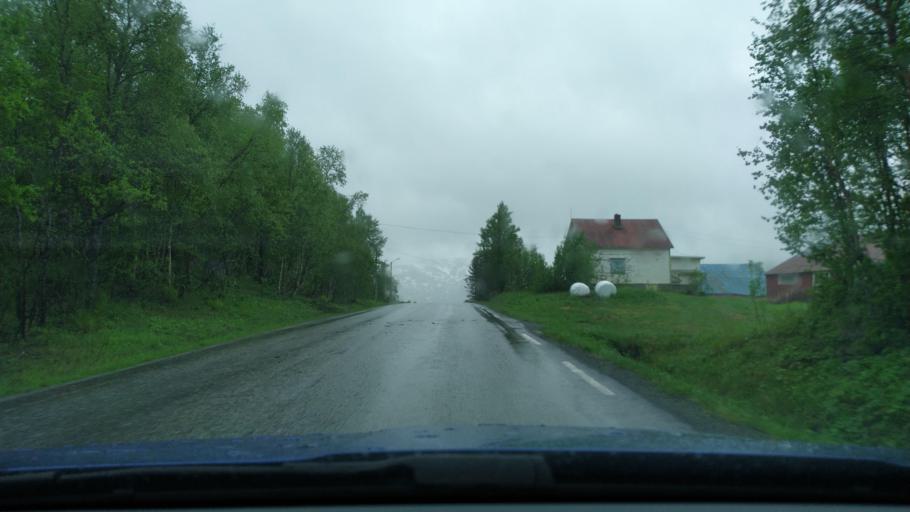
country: NO
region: Troms
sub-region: Dyroy
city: Brostadbotn
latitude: 69.0138
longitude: 17.7291
